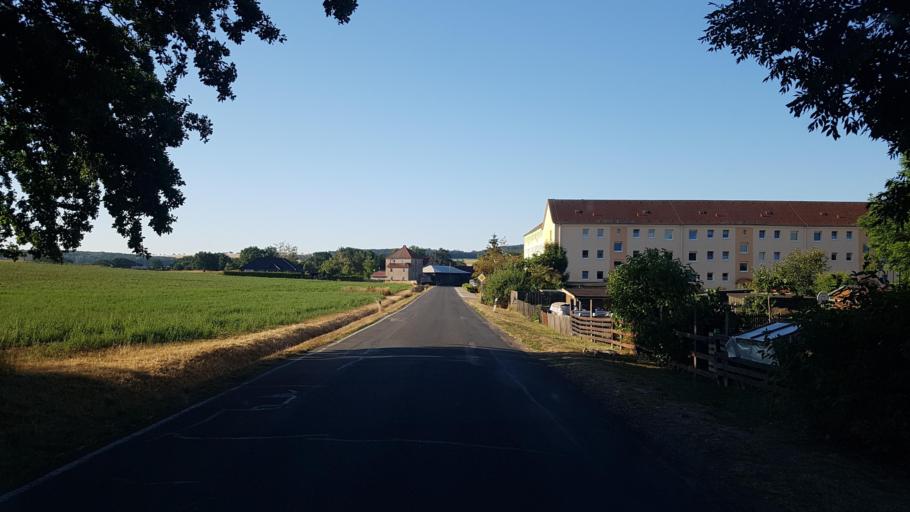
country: DE
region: Saxony
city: Dahlen
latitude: 51.3322
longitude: 13.0163
